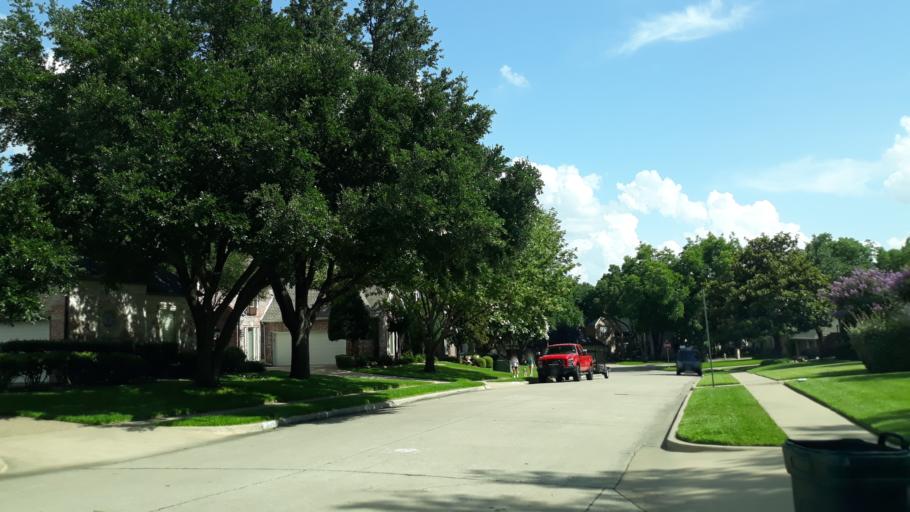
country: US
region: Texas
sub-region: Dallas County
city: Coppell
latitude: 32.9571
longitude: -97.0001
